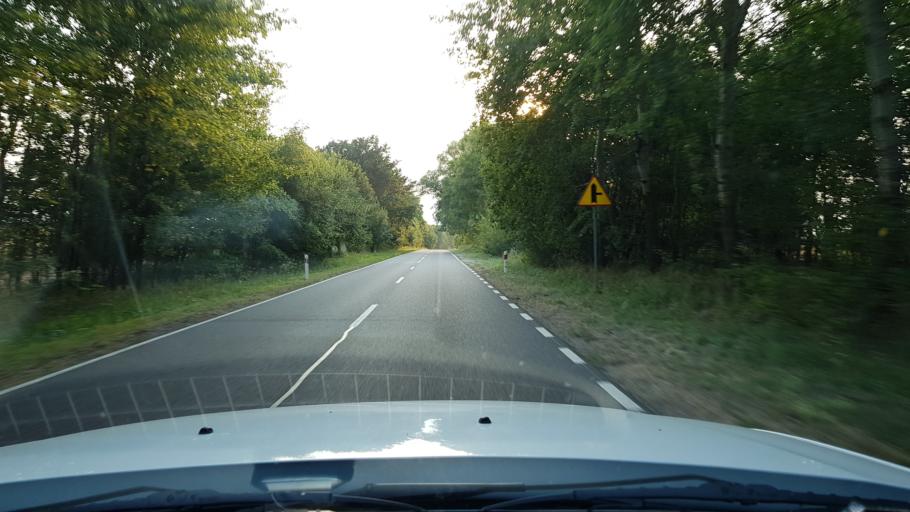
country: PL
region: West Pomeranian Voivodeship
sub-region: Powiat stargardzki
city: Marianowo
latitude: 53.4284
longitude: 15.2323
